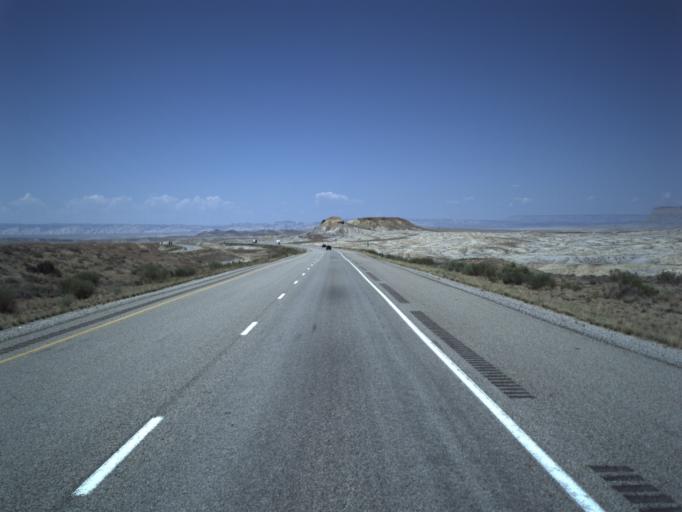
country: US
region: Utah
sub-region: Grand County
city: Moab
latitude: 38.9251
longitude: -109.9797
